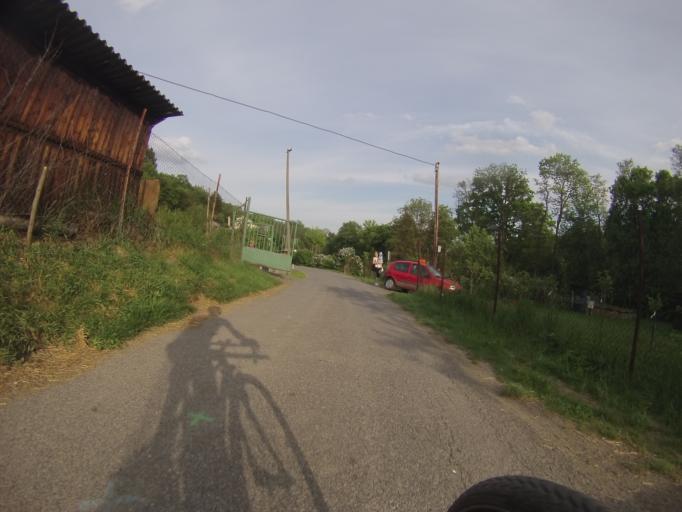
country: CZ
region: Olomoucky
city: Pteni
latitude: 49.4743
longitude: 16.9629
